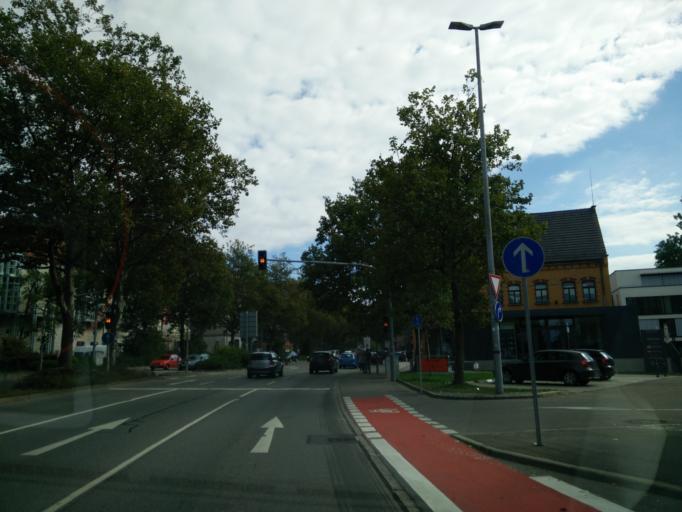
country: DE
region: Baden-Wuerttemberg
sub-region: Tuebingen Region
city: Reutlingen
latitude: 48.4903
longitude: 9.2093
